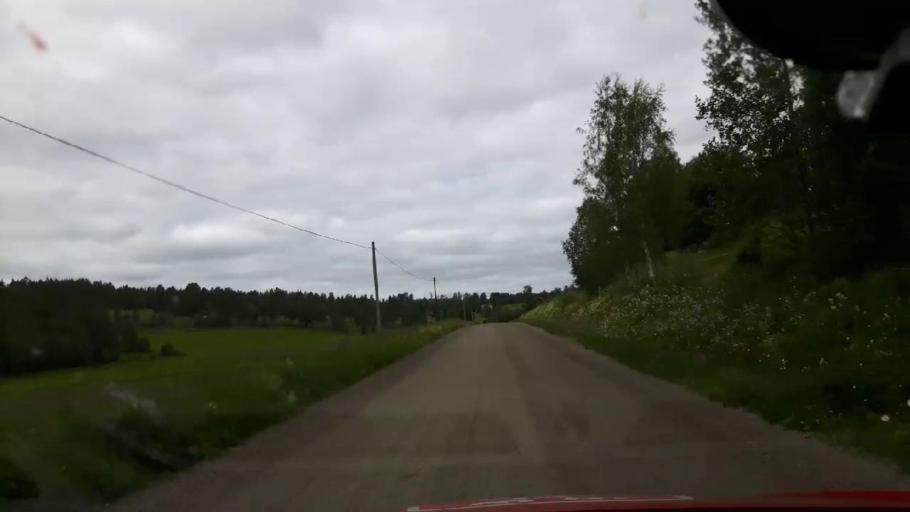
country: SE
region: Jaemtland
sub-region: OEstersunds Kommun
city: Brunflo
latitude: 62.9169
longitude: 15.0232
